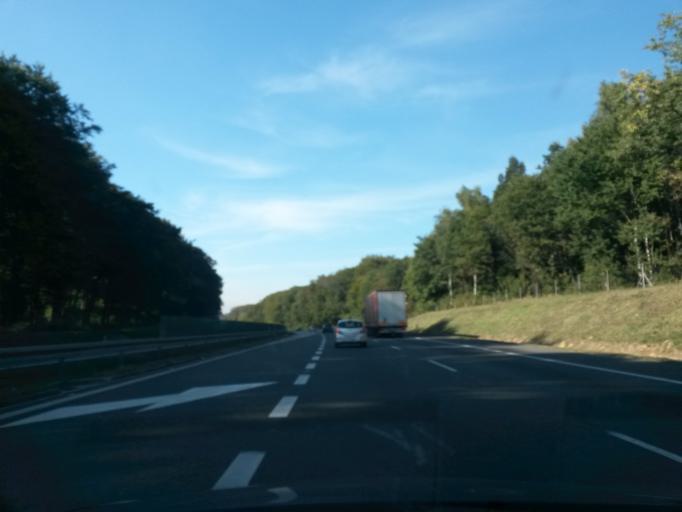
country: PL
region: Opole Voivodeship
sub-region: Powiat strzelecki
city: Lesnica
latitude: 50.4663
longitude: 18.1517
